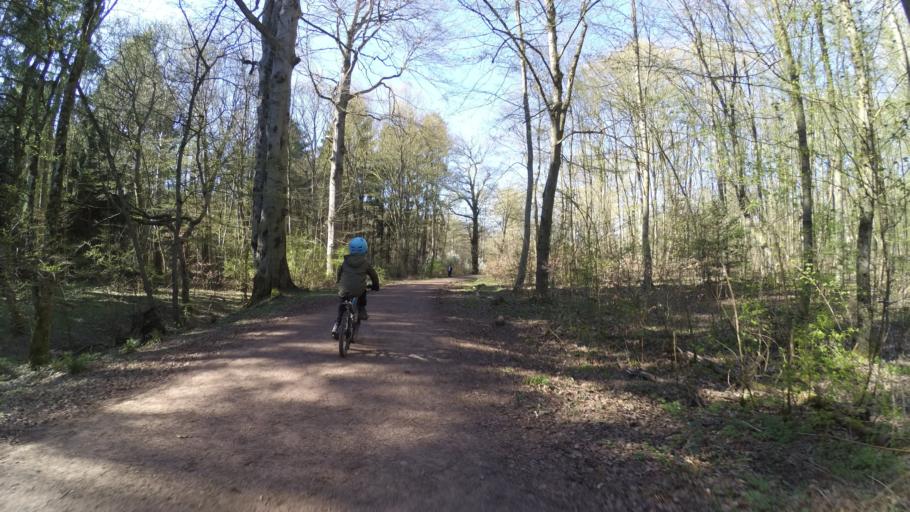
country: DE
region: Saarland
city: Volklingen
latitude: 49.2639
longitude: 6.8751
